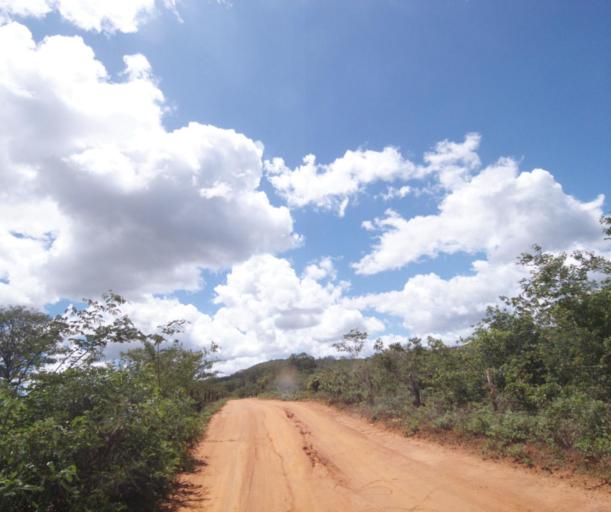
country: BR
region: Bahia
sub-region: Pocoes
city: Pocoes
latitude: -14.3901
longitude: -40.5281
